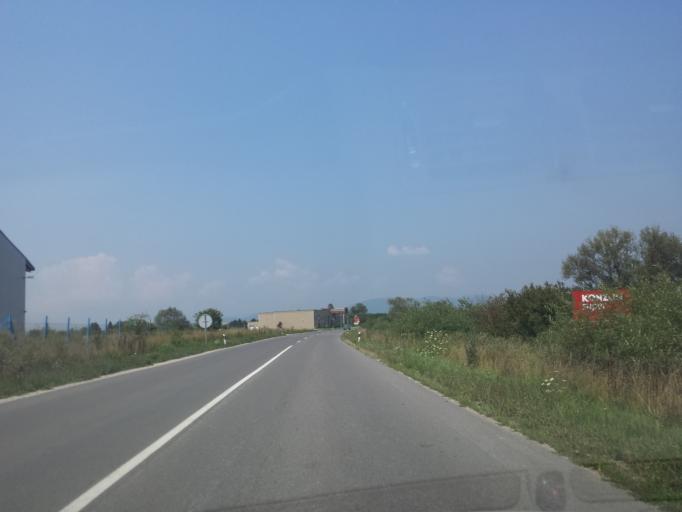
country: HR
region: Zagrebacka
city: Jastrebarsko
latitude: 45.6526
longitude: 15.6588
